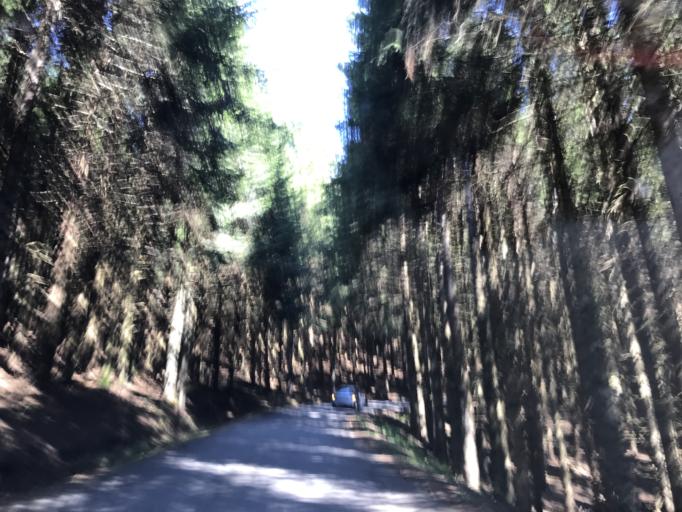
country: FR
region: Auvergne
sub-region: Departement du Puy-de-Dome
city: Job
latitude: 45.6772
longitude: 3.7591
